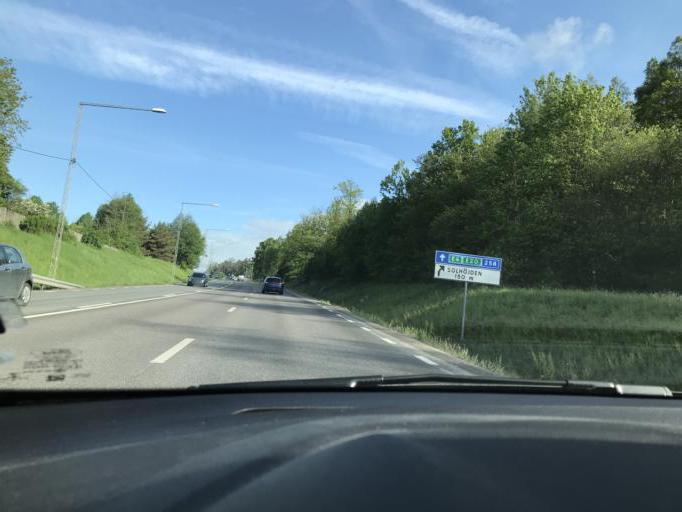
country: SE
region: Stockholm
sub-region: Botkyrka Kommun
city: Tumba
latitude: 59.2065
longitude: 17.8394
